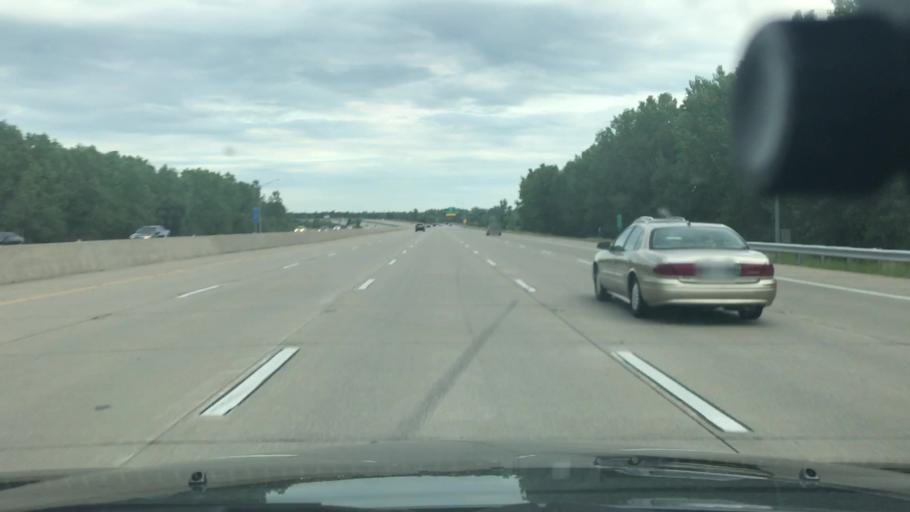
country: US
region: Missouri
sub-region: Saint Charles County
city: Saint Charles
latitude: 38.7150
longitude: -90.5084
